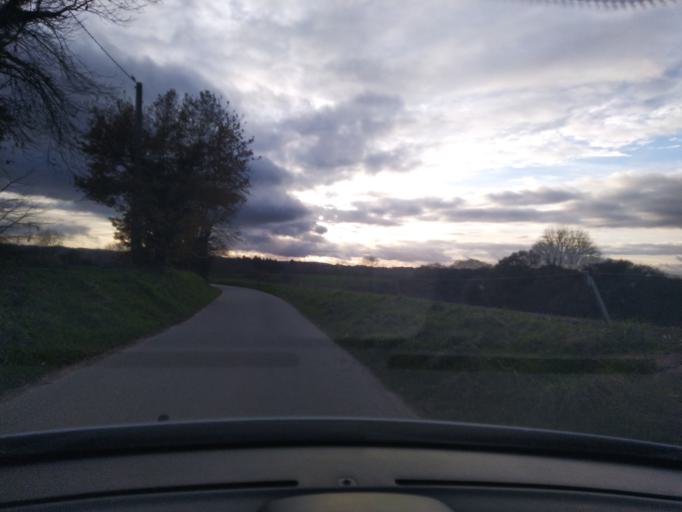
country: FR
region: Brittany
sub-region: Departement du Finistere
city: Guerlesquin
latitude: 48.5622
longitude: -3.6162
